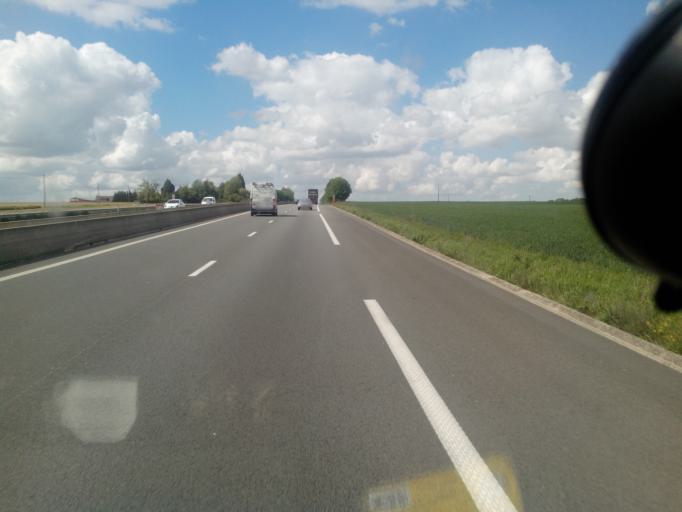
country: FR
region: Nord-Pas-de-Calais
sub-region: Departement du Nord
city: Godewaersvelde
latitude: 50.7634
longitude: 2.6406
